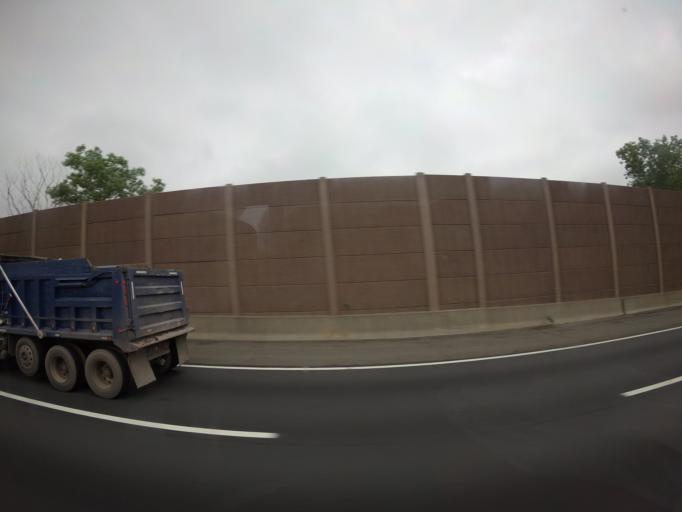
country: US
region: New Jersey
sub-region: Middlesex County
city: Carteret
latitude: 40.5826
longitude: -74.2418
